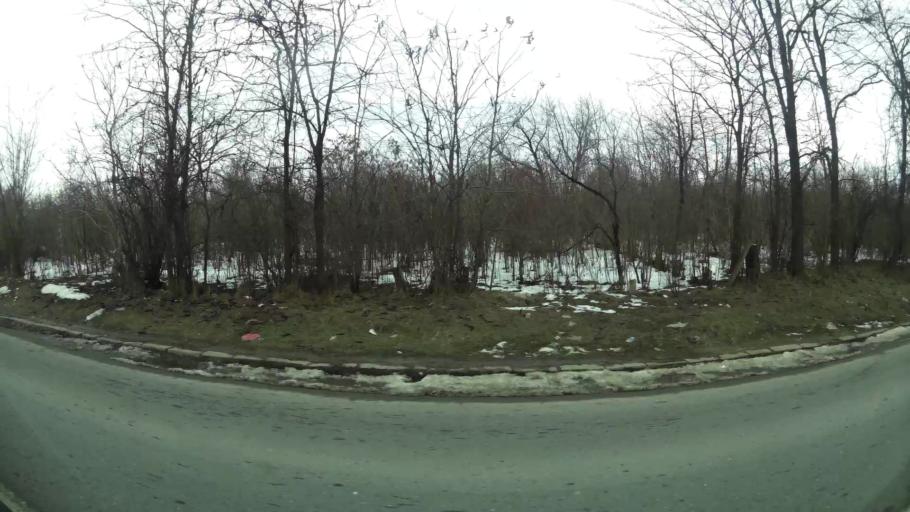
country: RS
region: Central Serbia
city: Sremcica
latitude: 44.7257
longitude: 20.3917
